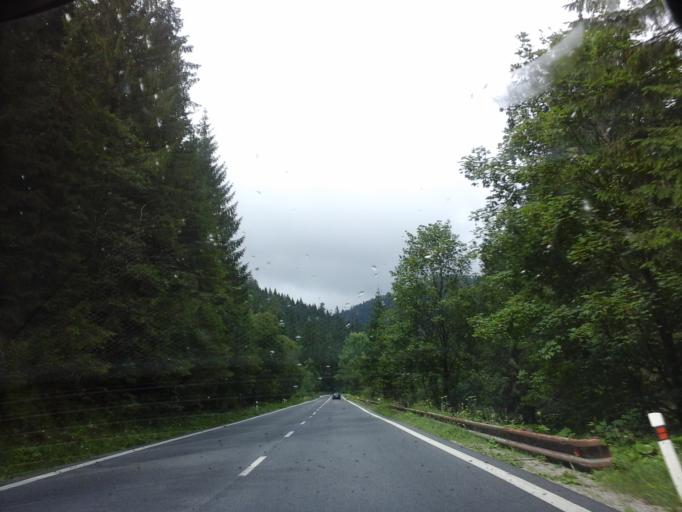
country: SK
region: Kosicky
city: Dobsina
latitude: 48.8783
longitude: 20.3196
